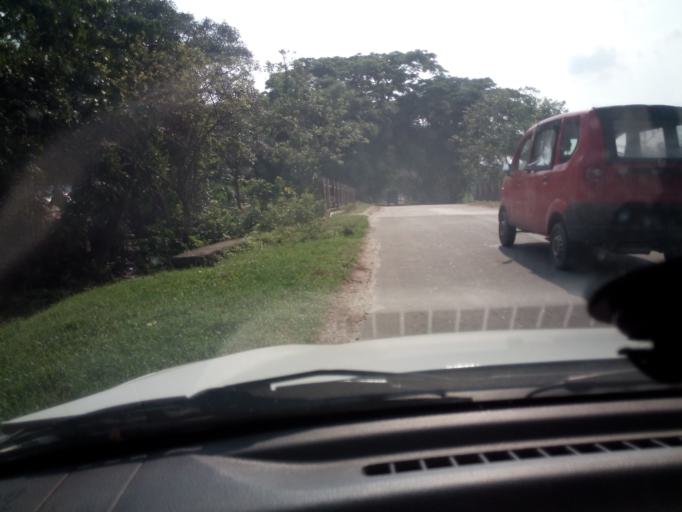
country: IN
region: Assam
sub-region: Udalguri
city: Udalguri
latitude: 26.7459
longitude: 92.1158
